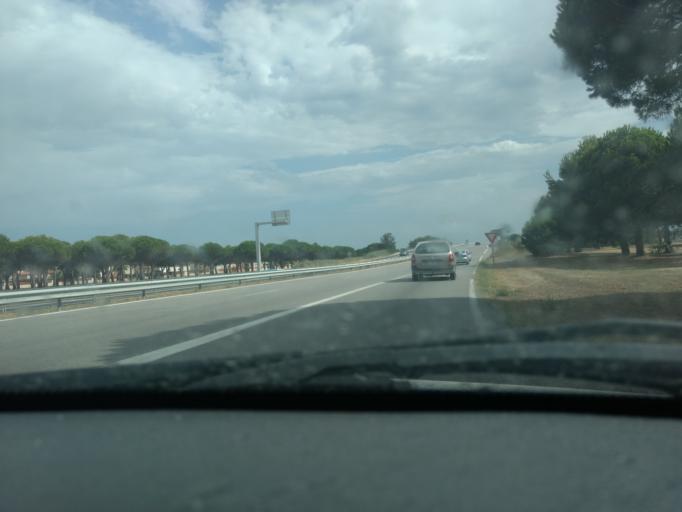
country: FR
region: Languedoc-Roussillon
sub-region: Departement des Pyrenees-Orientales
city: Le Barcares
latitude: 42.8093
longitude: 3.0309
